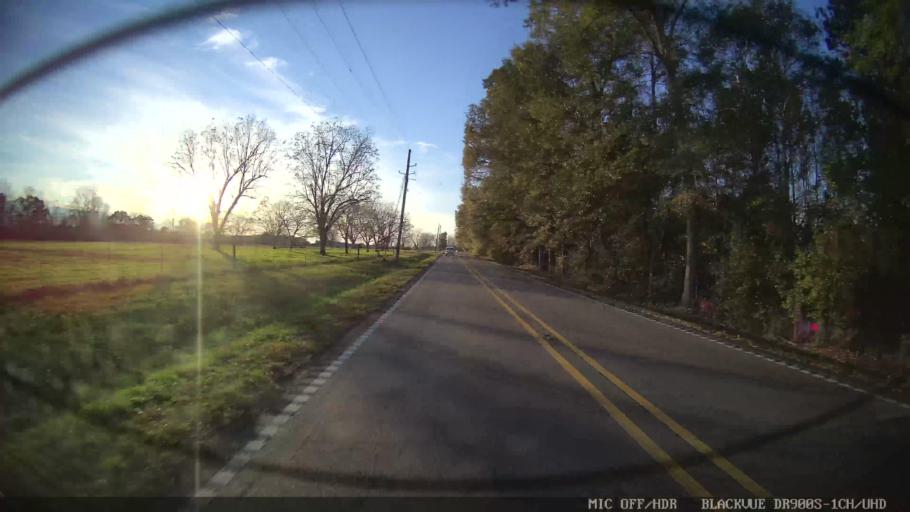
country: US
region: Mississippi
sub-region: Lamar County
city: Lumberton
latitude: 30.9957
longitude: -89.3872
